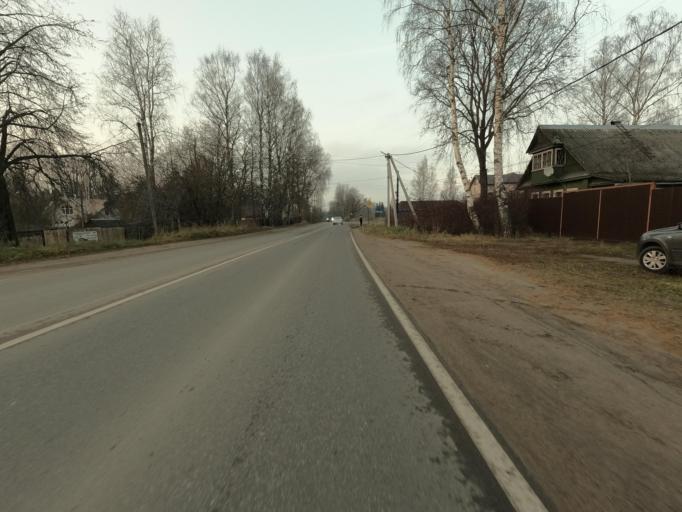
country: RU
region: Leningrad
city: Kirovsk
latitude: 59.8316
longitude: 30.9899
